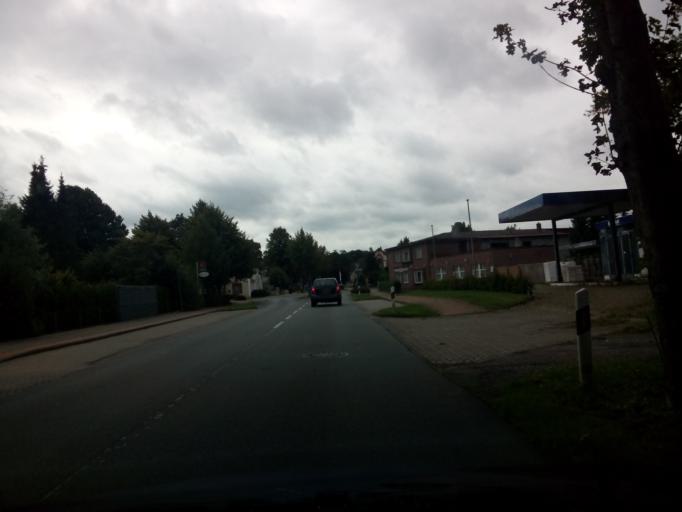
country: DE
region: Lower Saxony
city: Kohlen
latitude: 53.5089
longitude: 8.8589
